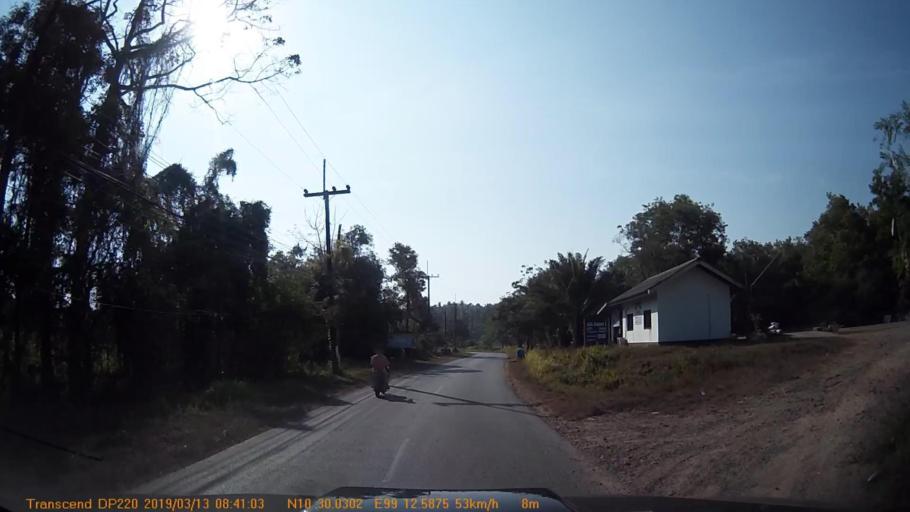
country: TH
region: Chumphon
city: Chumphon
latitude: 10.5004
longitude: 99.2099
